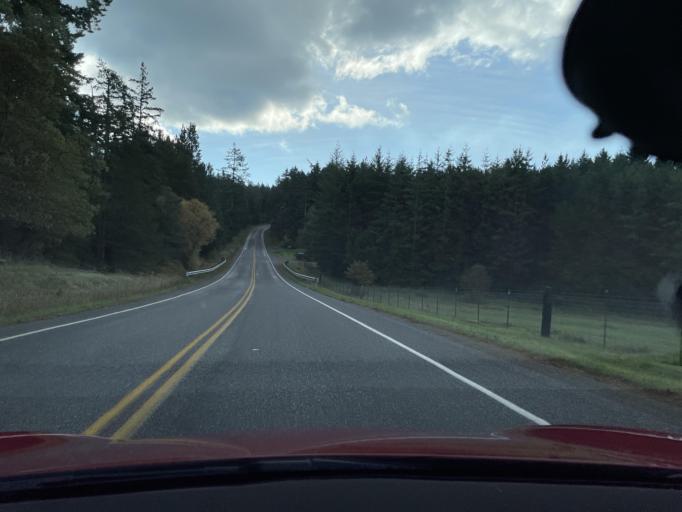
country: US
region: Washington
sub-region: San Juan County
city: Friday Harbor
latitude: 48.4920
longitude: -123.0323
